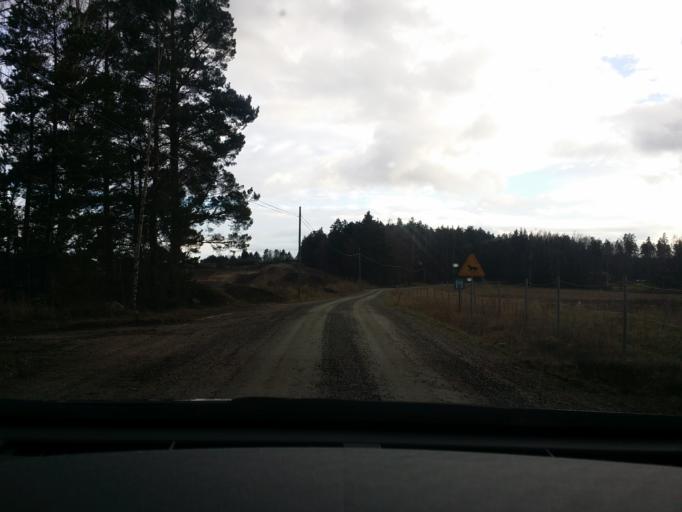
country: SE
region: Soedermanland
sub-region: Eskilstuna Kommun
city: Arla
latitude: 59.3739
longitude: 16.6744
